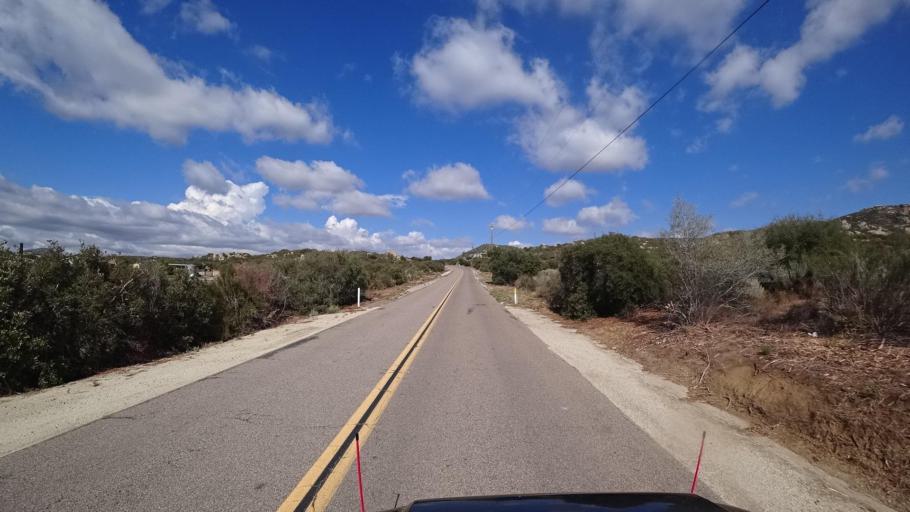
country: US
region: California
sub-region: San Diego County
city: Campo
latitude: 32.6868
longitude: -116.4945
